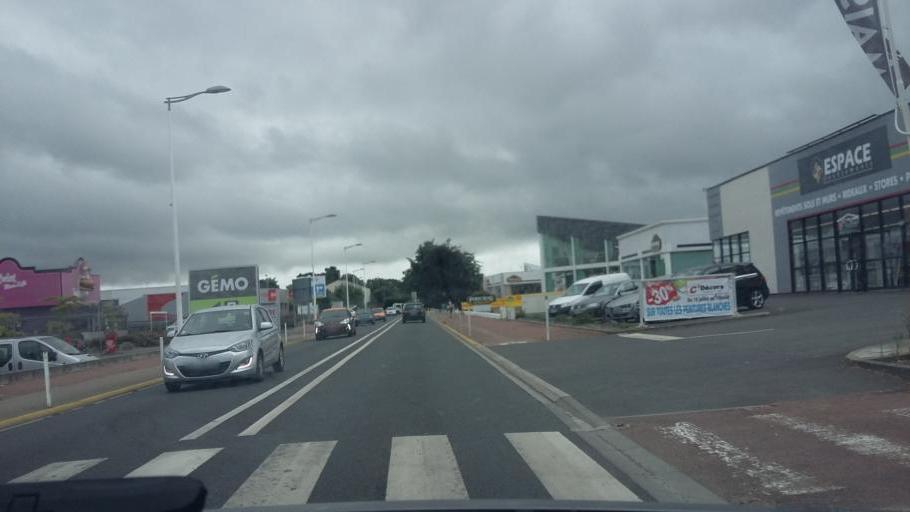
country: FR
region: Pays de la Loire
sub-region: Departement de la Vendee
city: Challans
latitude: 46.8522
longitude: -1.8918
